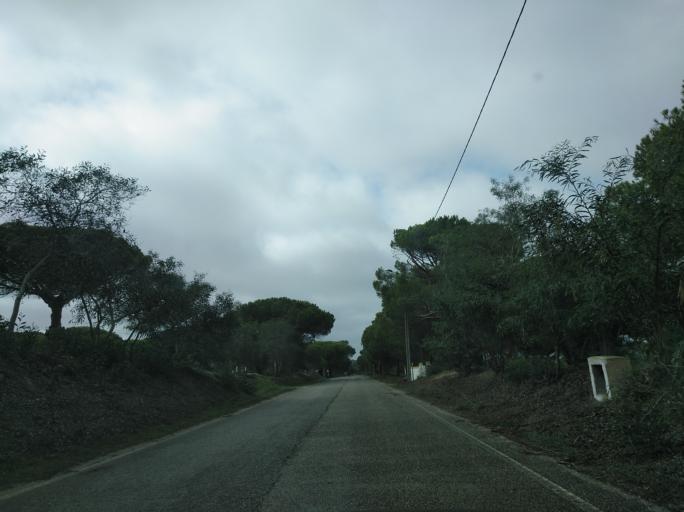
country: PT
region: Setubal
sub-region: Santiago do Cacem
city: Santo Andre
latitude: 38.1328
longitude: -8.7711
